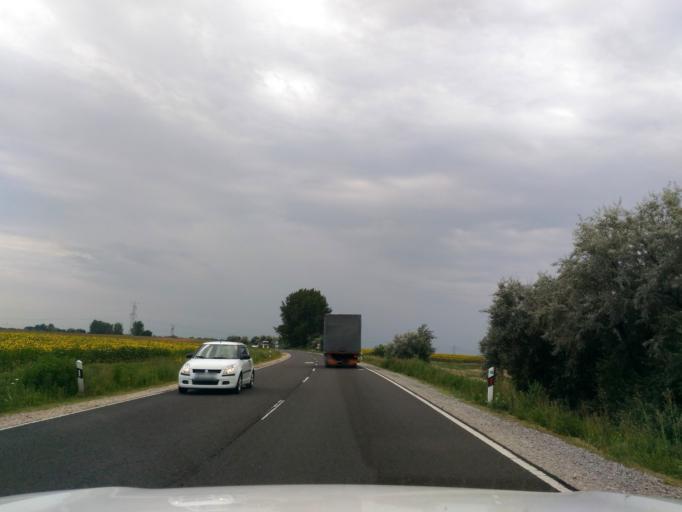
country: HU
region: Jasz-Nagykun-Szolnok
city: Toszeg
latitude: 47.1644
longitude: 20.1053
